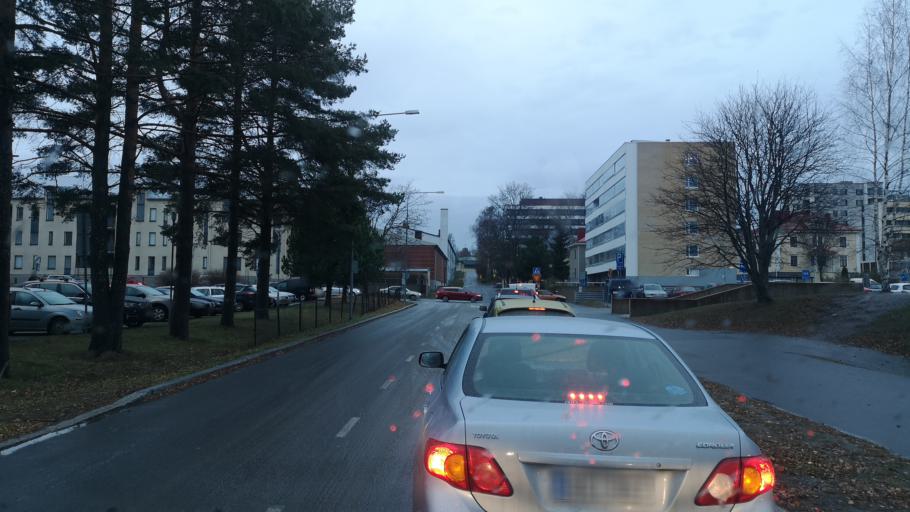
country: FI
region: Ostrobothnia
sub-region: Vaasa
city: Vaasa
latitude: 63.0863
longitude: 21.6193
